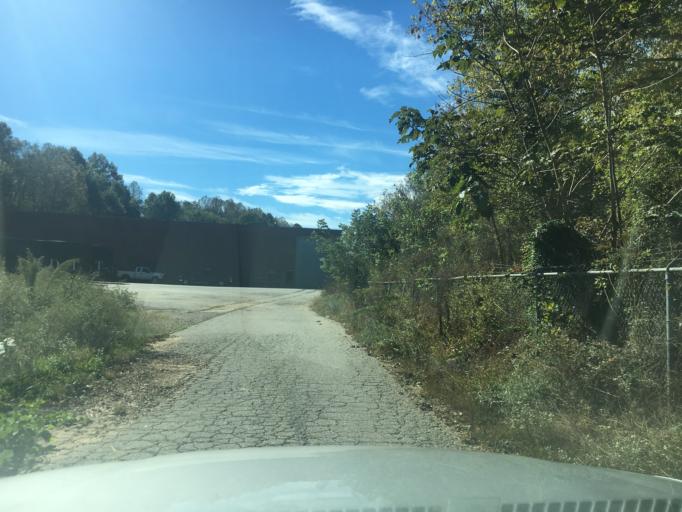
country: US
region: North Carolina
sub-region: Caldwell County
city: Lenoir
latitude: 35.9064
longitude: -81.5490
